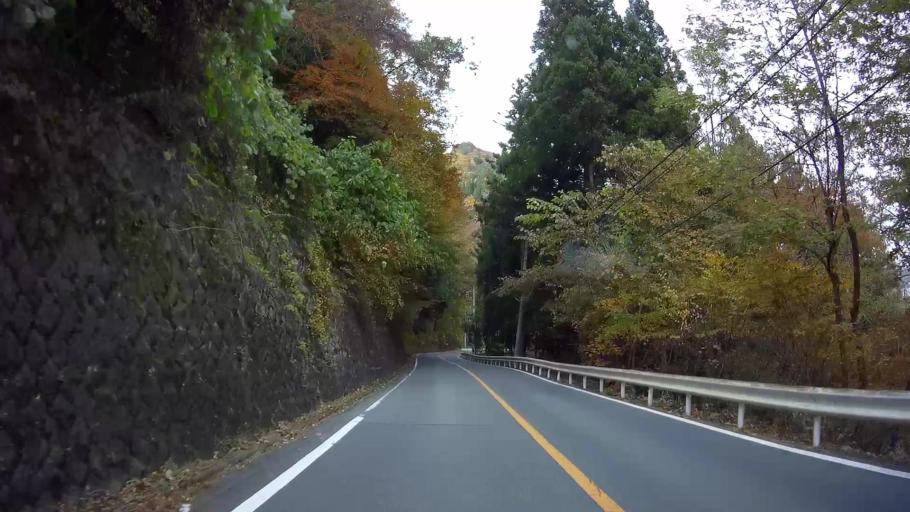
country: JP
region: Gunma
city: Nakanojomachi
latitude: 36.5908
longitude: 138.6258
